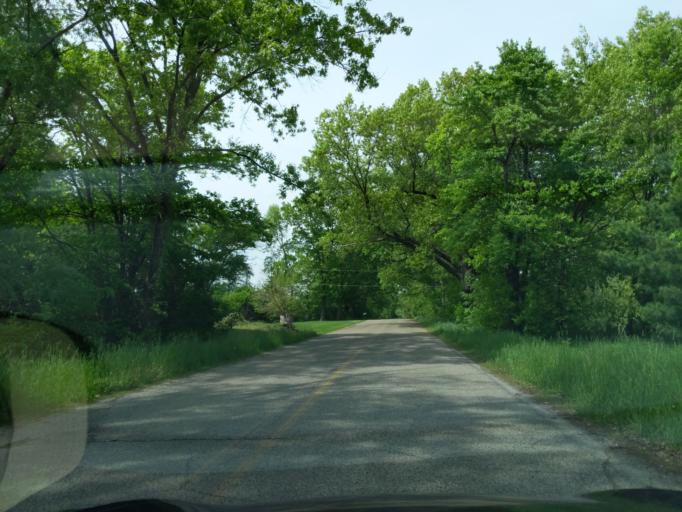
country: US
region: Michigan
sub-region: Ingham County
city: Leslie
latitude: 42.4122
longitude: -84.3334
